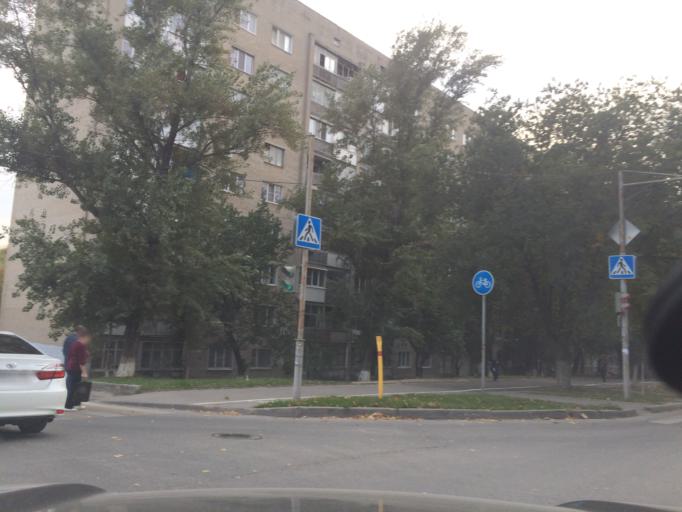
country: RU
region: Rostov
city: Rostov-na-Donu
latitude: 47.2077
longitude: 39.6214
